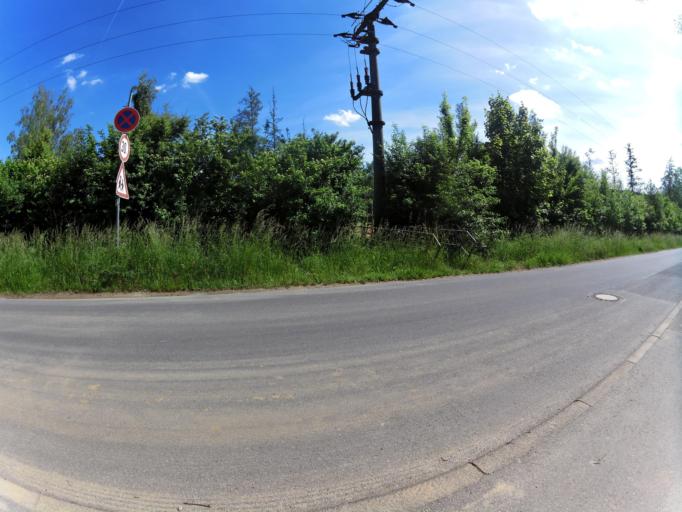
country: DE
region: Bavaria
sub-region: Regierungsbezirk Unterfranken
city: Uettingen
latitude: 49.7939
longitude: 9.7333
